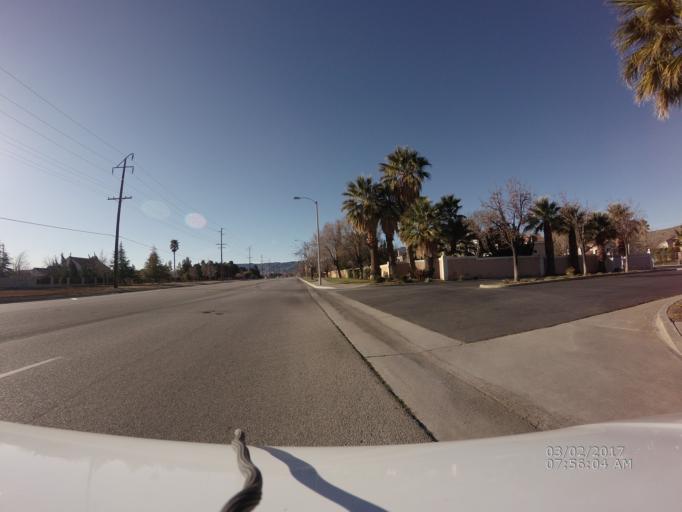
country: US
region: California
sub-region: Los Angeles County
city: Desert View Highlands
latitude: 34.6149
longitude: -118.1838
